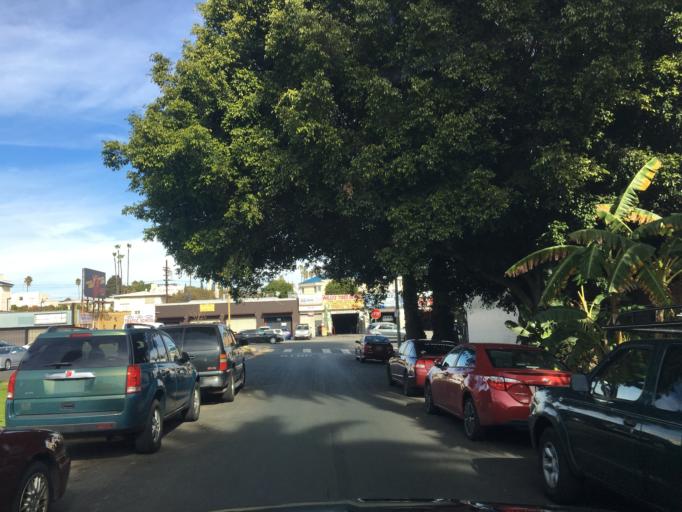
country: US
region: California
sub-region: Los Angeles County
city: Silver Lake
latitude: 34.0704
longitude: -118.2803
